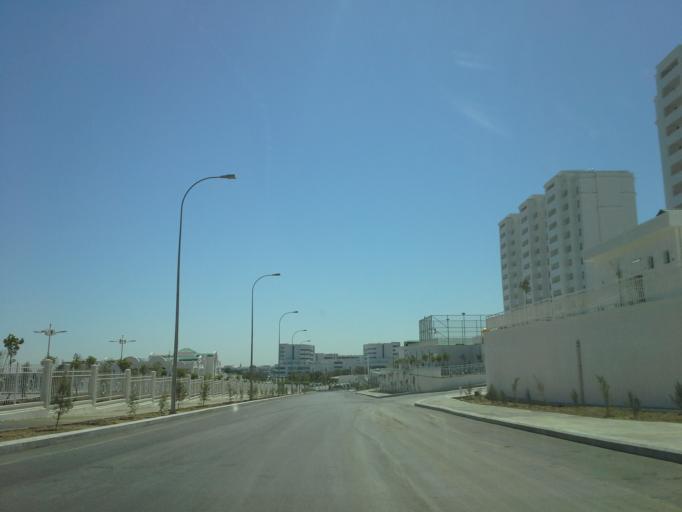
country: TM
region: Ahal
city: Ashgabat
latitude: 37.9427
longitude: 58.3522
